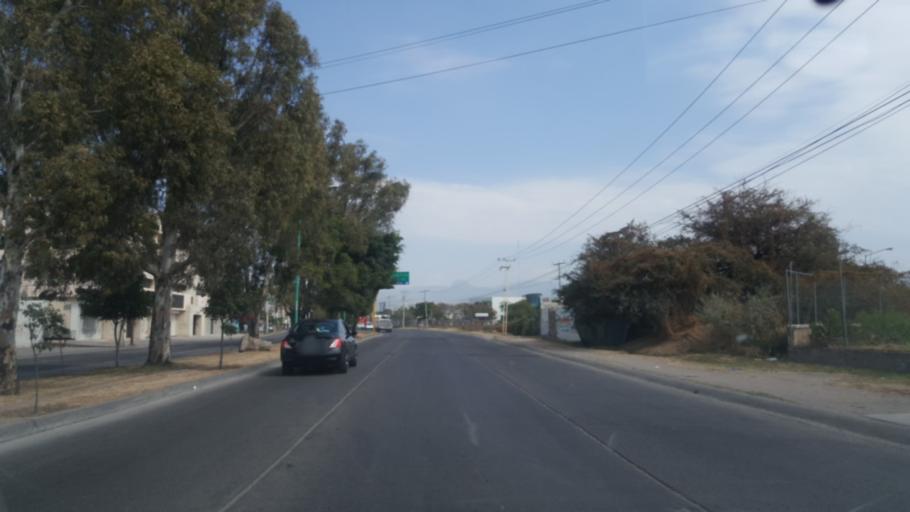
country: MX
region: Guanajuato
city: Leon
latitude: 21.1019
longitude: -101.6607
